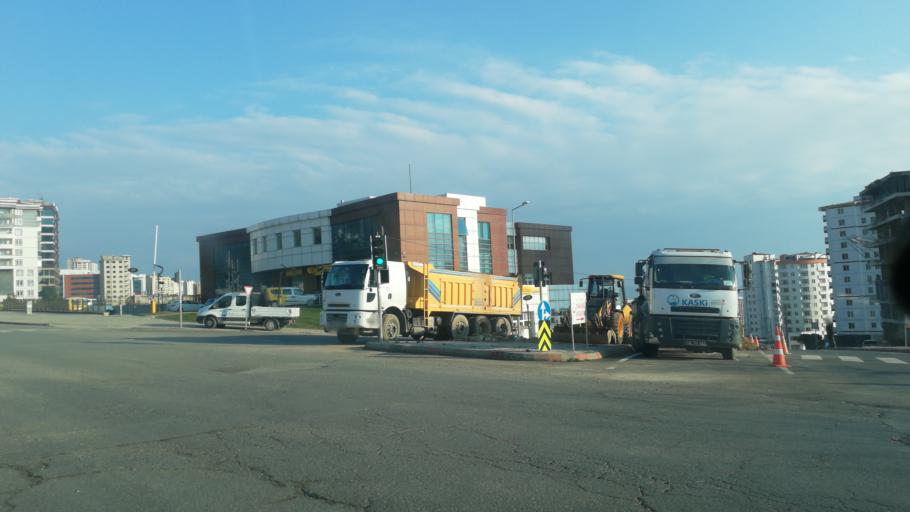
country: TR
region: Kahramanmaras
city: Kahramanmaras
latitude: 37.5999
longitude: 36.8315
